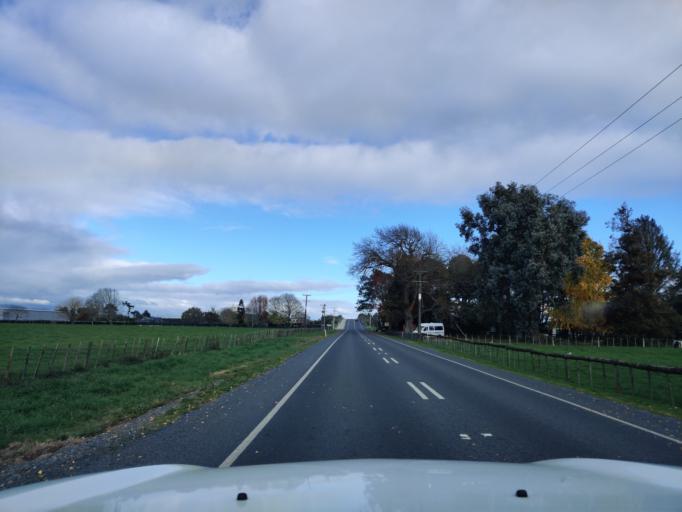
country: NZ
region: Waikato
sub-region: Waipa District
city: Cambridge
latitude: -37.8640
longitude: 175.4390
